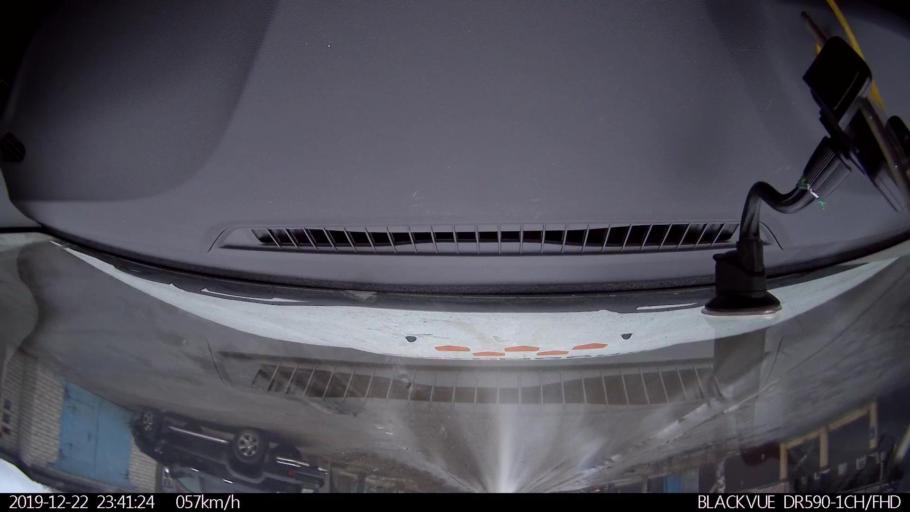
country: RU
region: Nizjnij Novgorod
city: Nizhniy Novgorod
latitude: 56.2850
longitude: 43.9118
